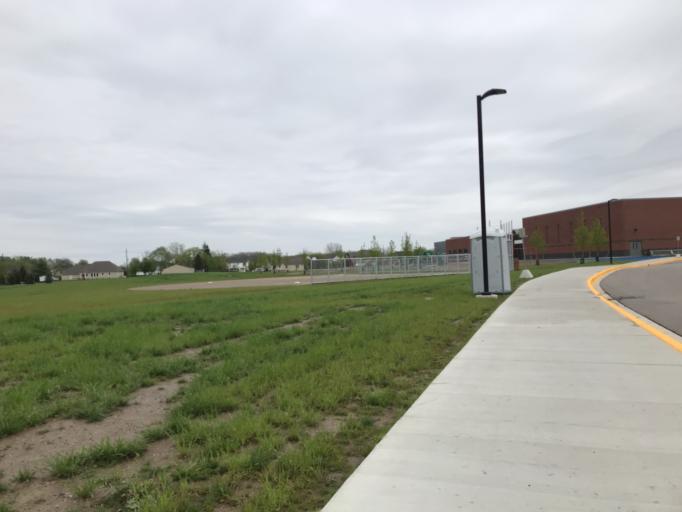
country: US
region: Michigan
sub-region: Oakland County
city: South Lyon
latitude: 42.4783
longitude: -83.6222
